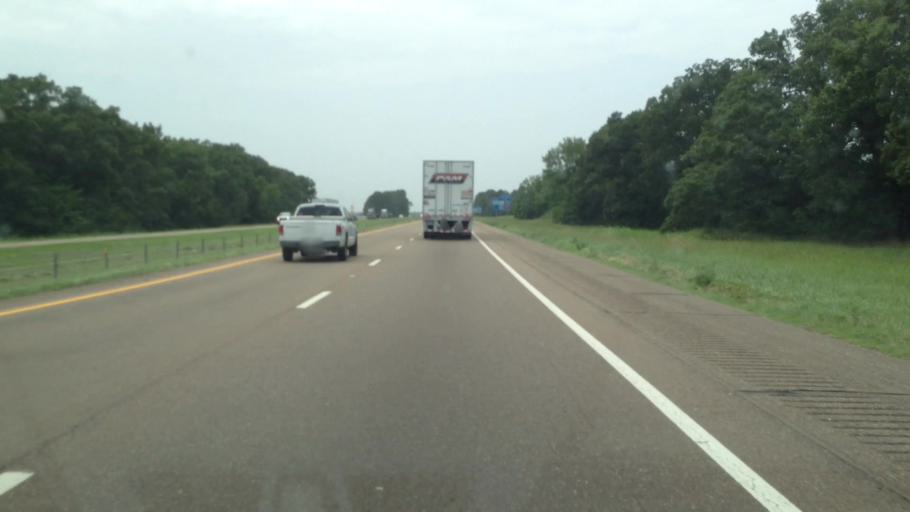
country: US
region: Texas
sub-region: Bowie County
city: New Boston
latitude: 33.4726
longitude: -94.3877
